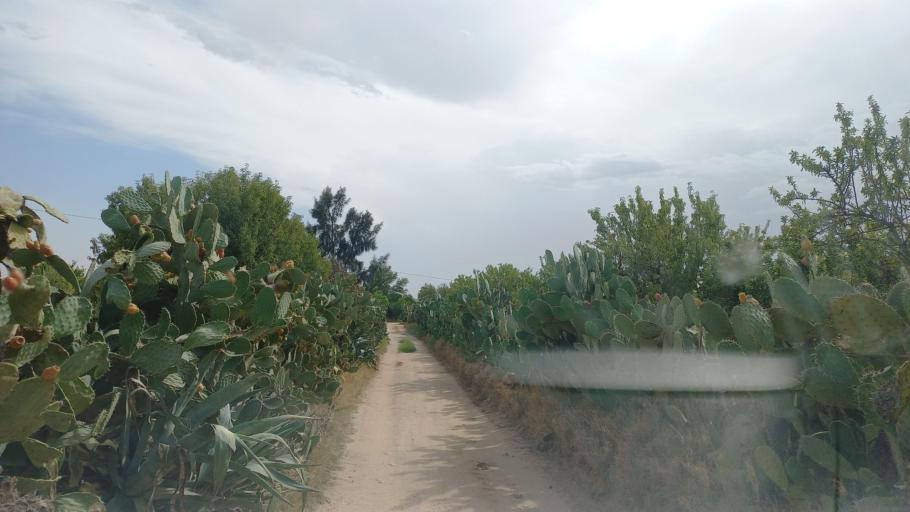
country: TN
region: Al Qasrayn
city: Kasserine
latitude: 35.2477
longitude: 9.0109
